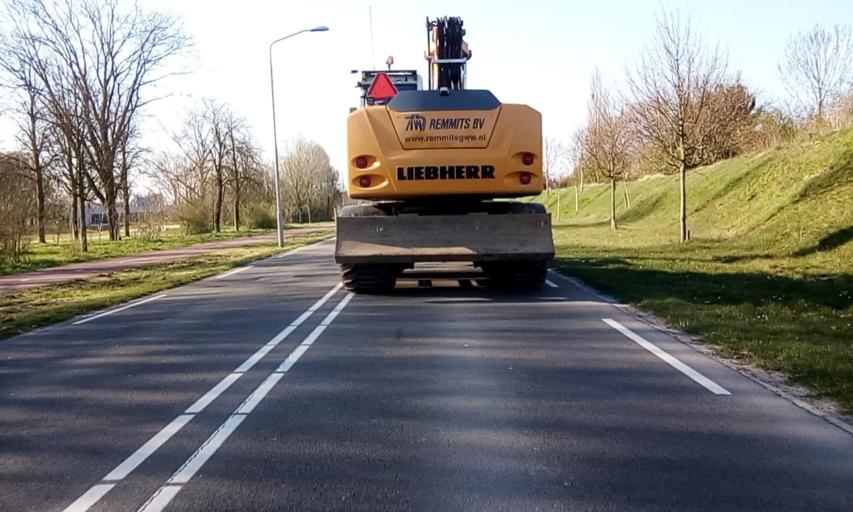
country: NL
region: Gelderland
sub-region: Gemeente Wijchen
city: Wijchen
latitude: 51.8018
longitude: 5.7351
